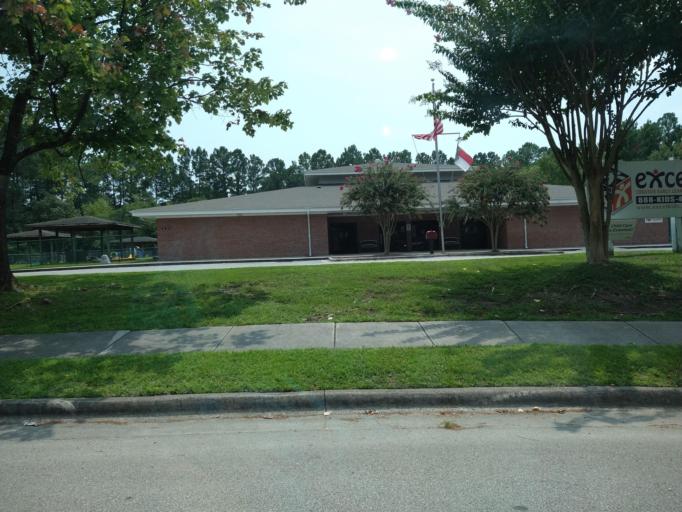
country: US
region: North Carolina
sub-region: Onslow County
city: Pumpkin Center
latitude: 34.7607
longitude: -77.3799
